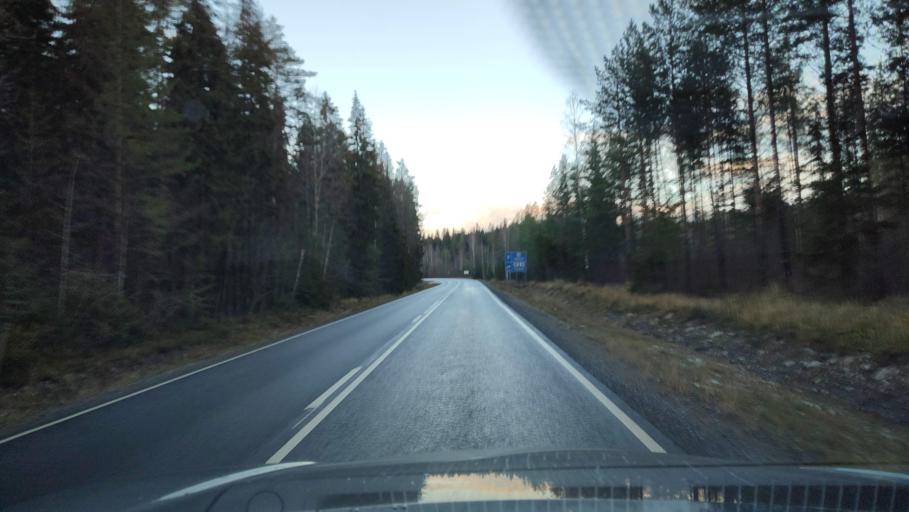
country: FI
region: Southern Ostrobothnia
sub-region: Suupohja
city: Karijoki
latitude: 62.2825
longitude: 21.6190
